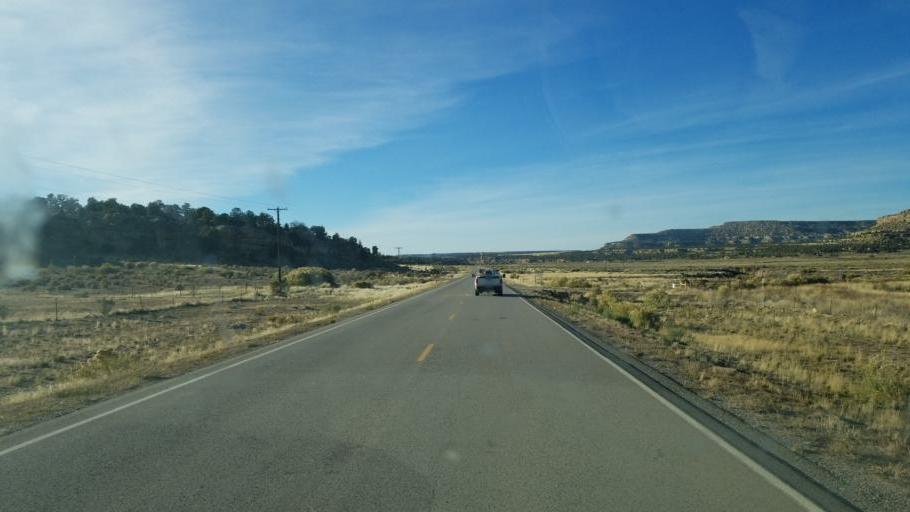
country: US
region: New Mexico
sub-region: San Juan County
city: Bloomfield
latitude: 36.7429
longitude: -107.5796
